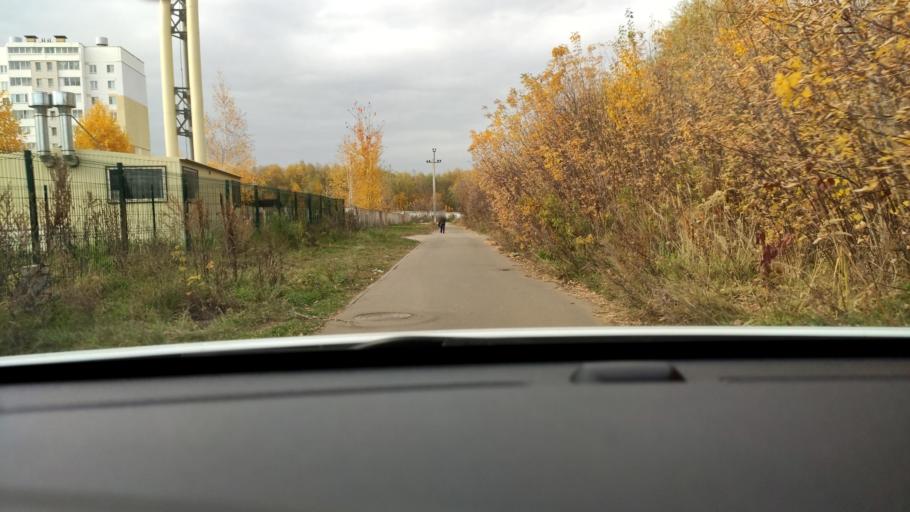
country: RU
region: Tatarstan
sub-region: Gorod Kazan'
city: Kazan
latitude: 55.8065
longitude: 49.2133
